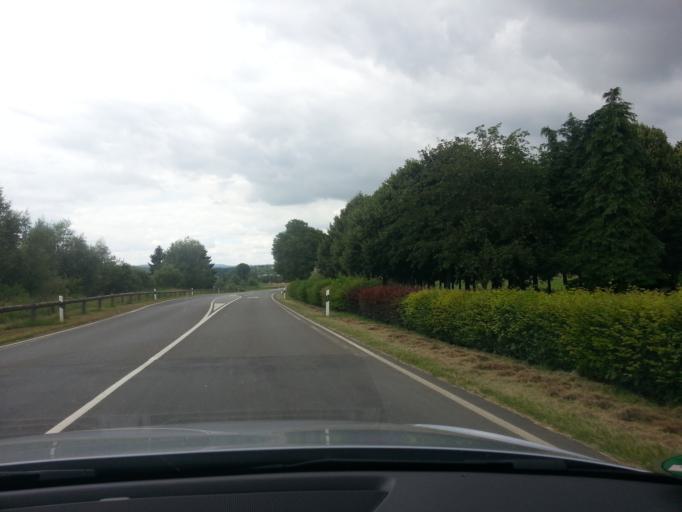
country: LU
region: Grevenmacher
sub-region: Canton de Remich
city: Mondorf-les-Bains
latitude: 49.5151
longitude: 6.3032
